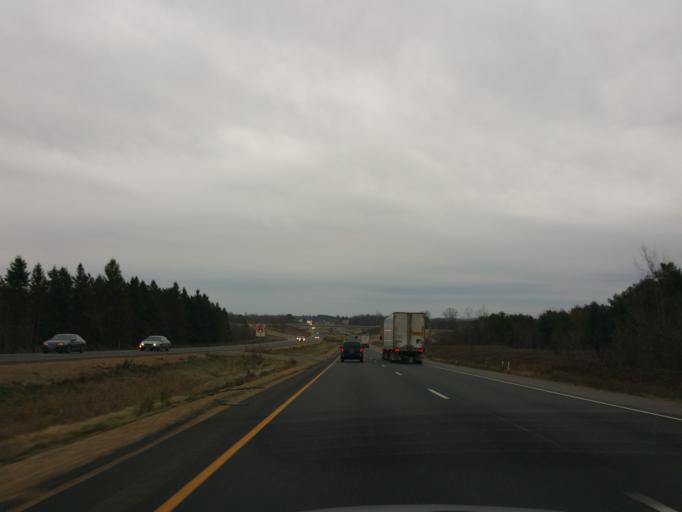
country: US
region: Wisconsin
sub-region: Saint Croix County
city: Woodville
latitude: 44.9347
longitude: -92.2867
